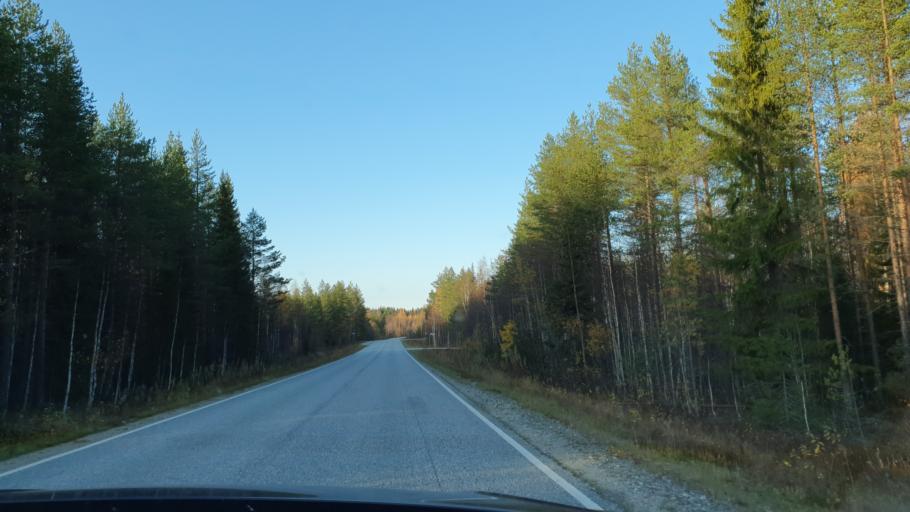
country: FI
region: Kainuu
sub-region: Kehys-Kainuu
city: Kuhmo
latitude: 64.3988
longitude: 29.4680
